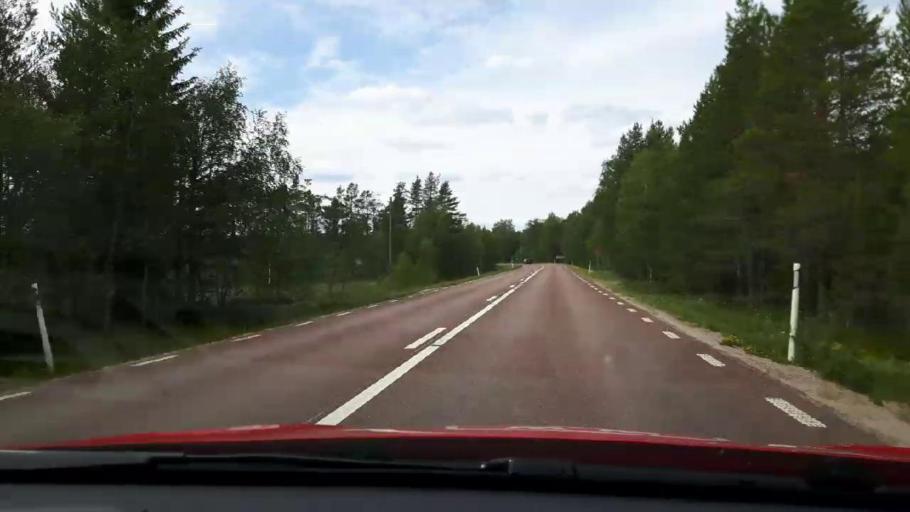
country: SE
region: Jaemtland
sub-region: Harjedalens Kommun
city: Sveg
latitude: 62.0594
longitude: 14.5798
